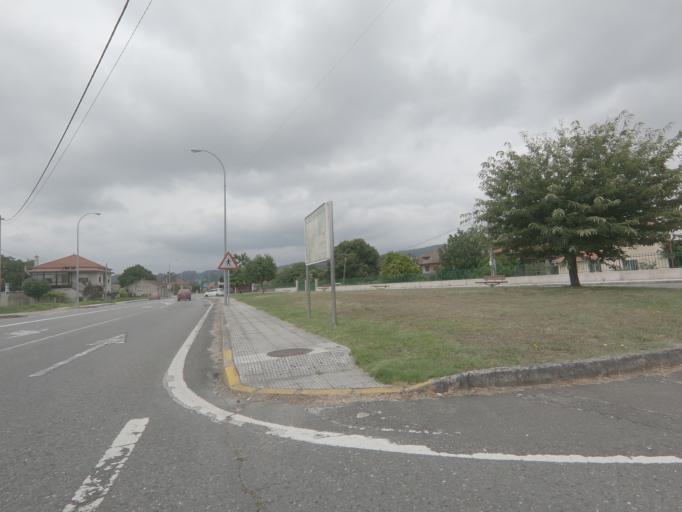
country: PT
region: Viana do Castelo
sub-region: Valenca
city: Valenca
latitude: 42.0391
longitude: -8.6525
